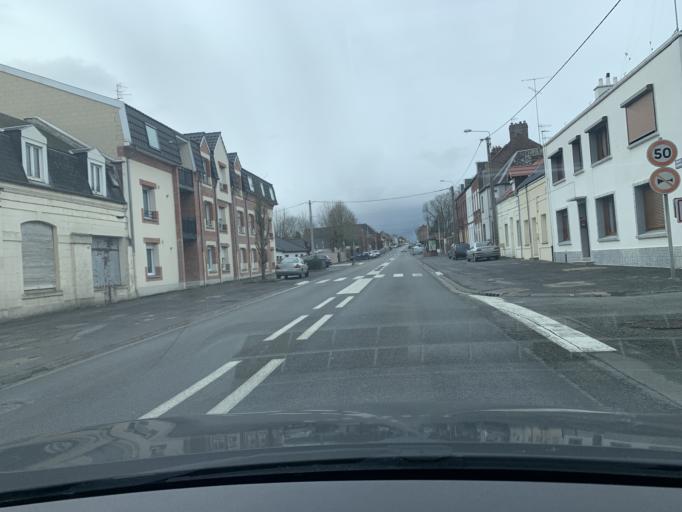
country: FR
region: Nord-Pas-de-Calais
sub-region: Departement du Nord
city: Neuville-Saint-Remy
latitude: 50.1800
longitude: 3.2077
